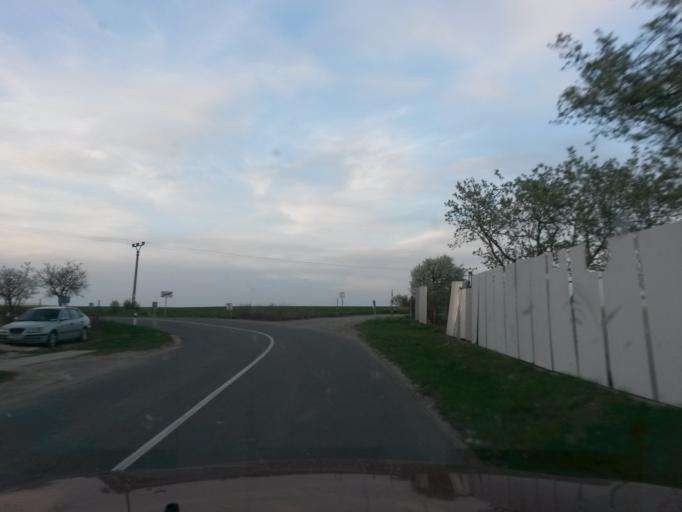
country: SK
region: Kosicky
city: Trebisov
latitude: 48.5506
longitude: 21.5581
